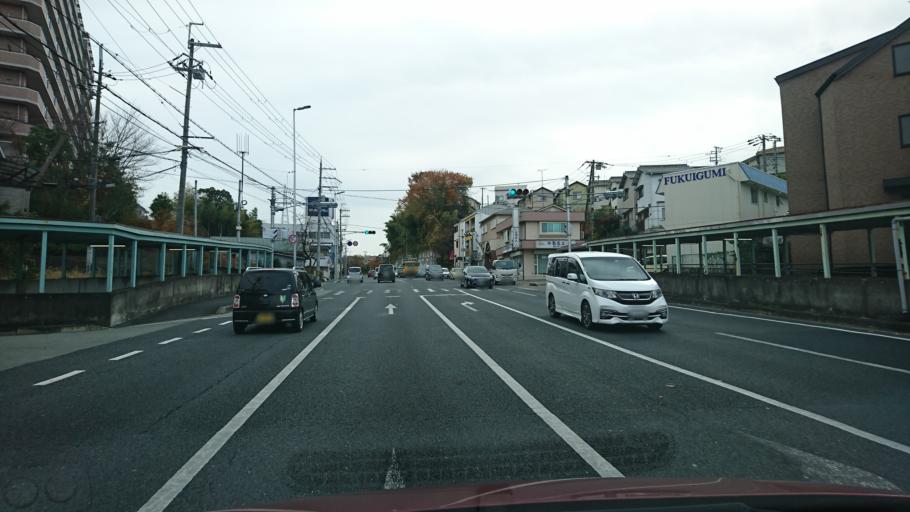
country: JP
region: Osaka
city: Ikeda
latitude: 34.8839
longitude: 135.4150
